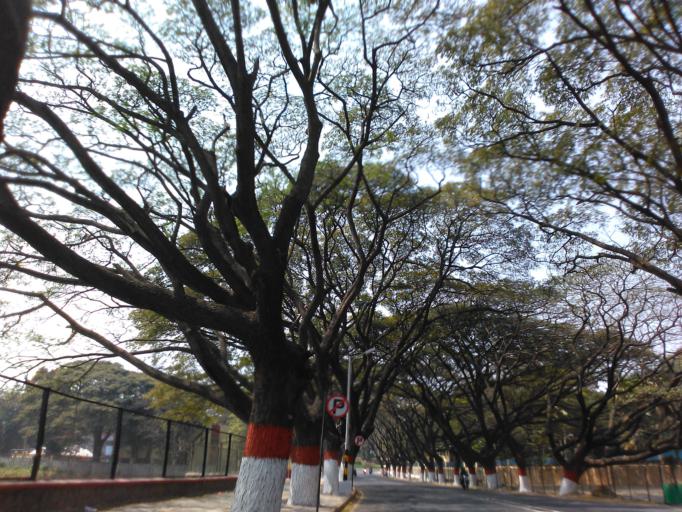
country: IN
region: Karnataka
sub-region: Bangalore Urban
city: Bangalore
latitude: 12.9801
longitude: 77.6549
